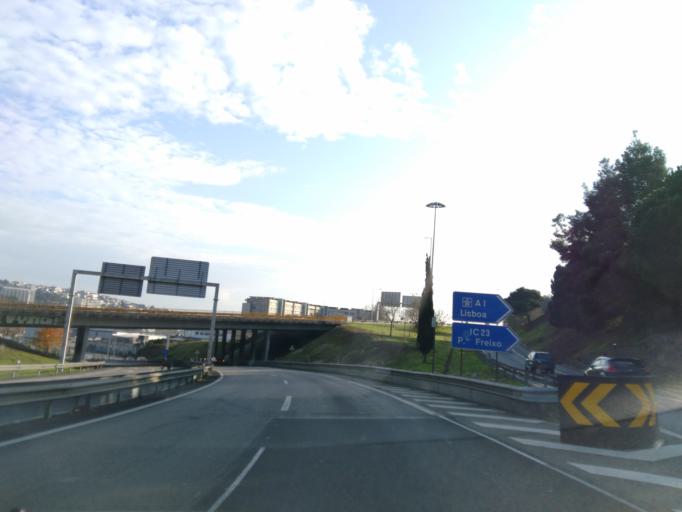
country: PT
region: Porto
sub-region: Gondomar
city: Valbom
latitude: 41.1477
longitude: -8.5814
